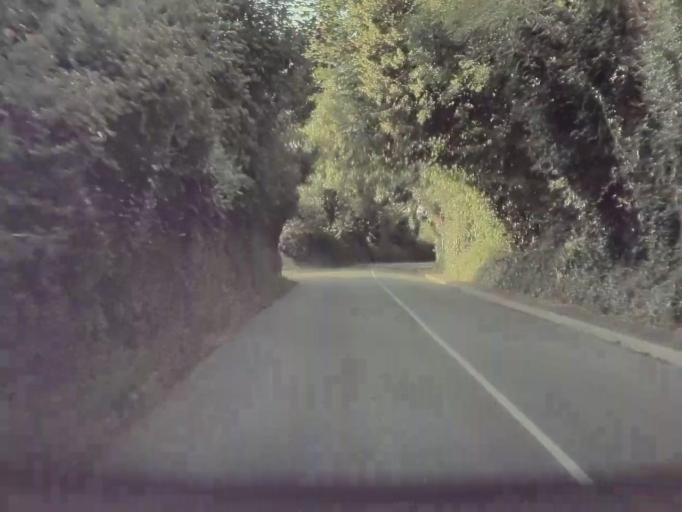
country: IE
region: Leinster
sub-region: Wicklow
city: Enniskerry
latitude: 53.2008
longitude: -6.1770
